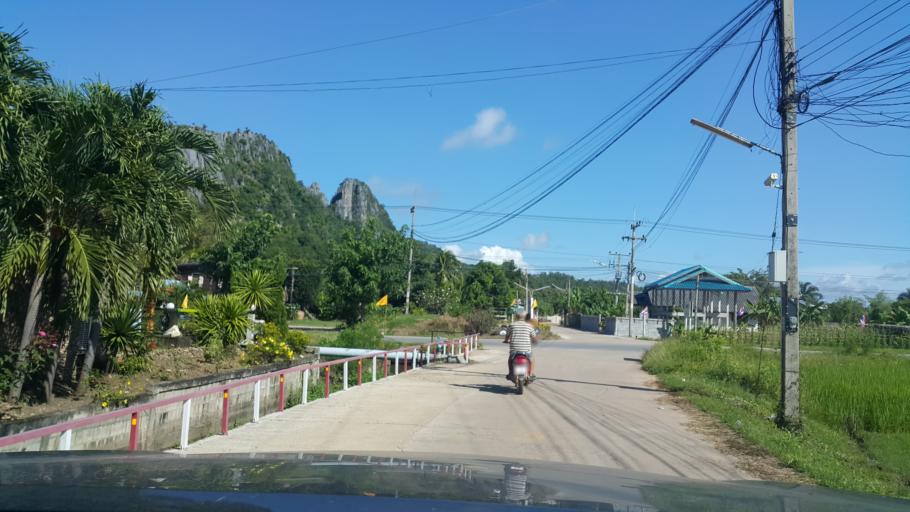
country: TH
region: Sukhothai
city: Thung Saliam
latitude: 17.3276
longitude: 99.5109
